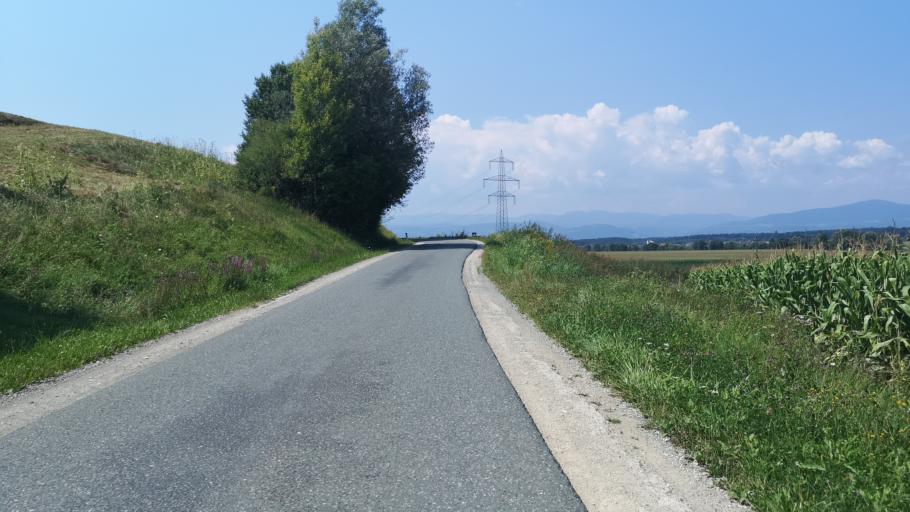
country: AT
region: Styria
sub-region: Politischer Bezirk Deutschlandsberg
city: Wettmannstatten
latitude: 46.8288
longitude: 15.3755
